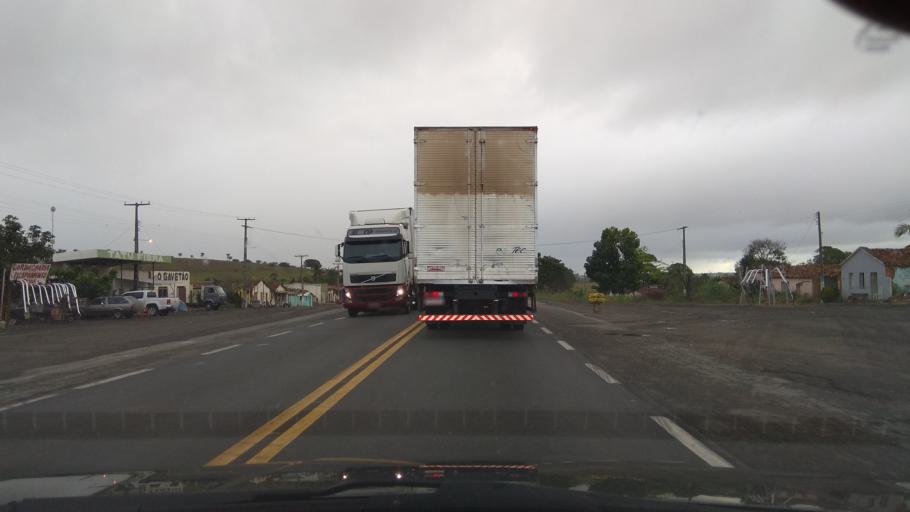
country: BR
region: Bahia
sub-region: Jaguaquara
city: Jaguaquara
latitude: -13.4797
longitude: -40.0418
